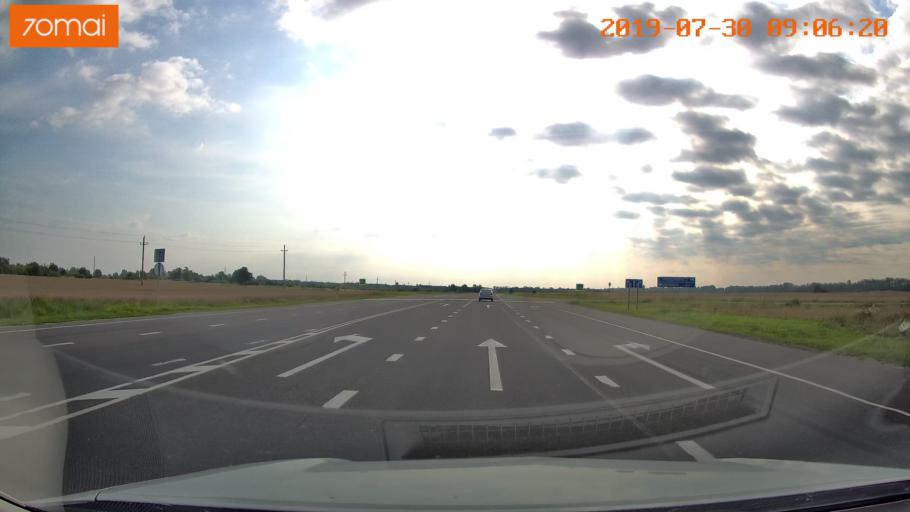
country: RU
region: Kaliningrad
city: Gusev
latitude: 54.6092
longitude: 22.3335
